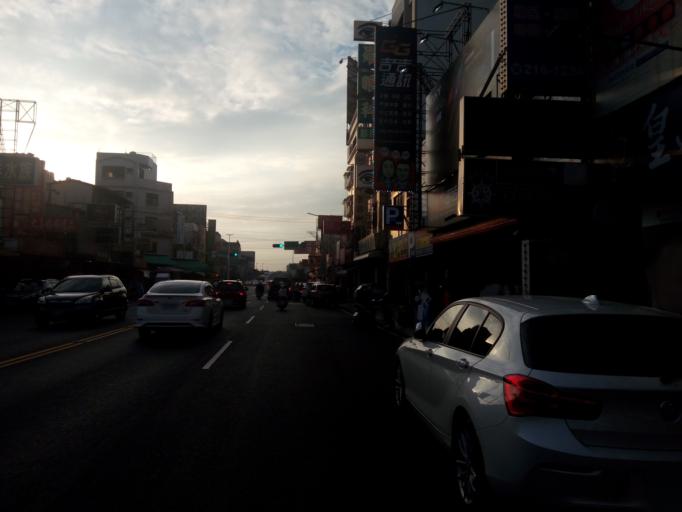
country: TW
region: Taiwan
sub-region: Chiayi
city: Jiayi Shi
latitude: 23.4752
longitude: 120.4408
